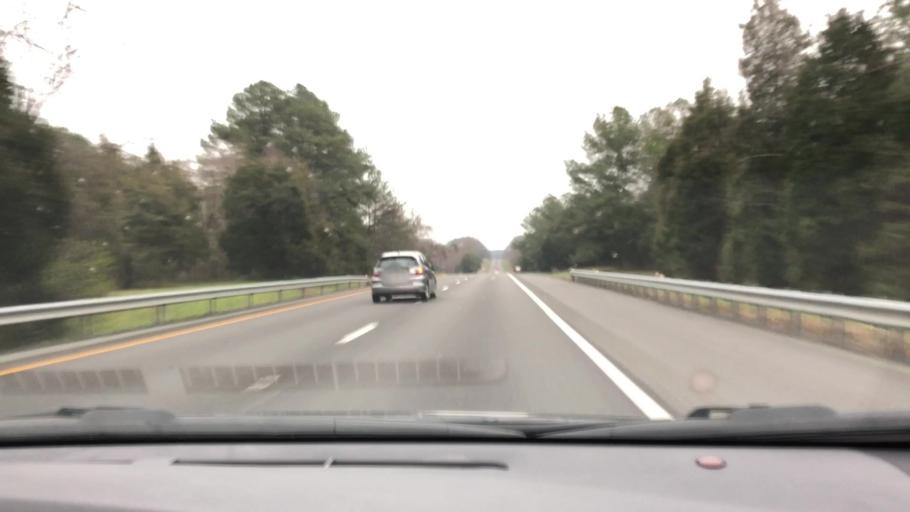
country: US
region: Virginia
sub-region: Fluvanna County
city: Lake Monticello
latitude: 37.9960
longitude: -78.2784
